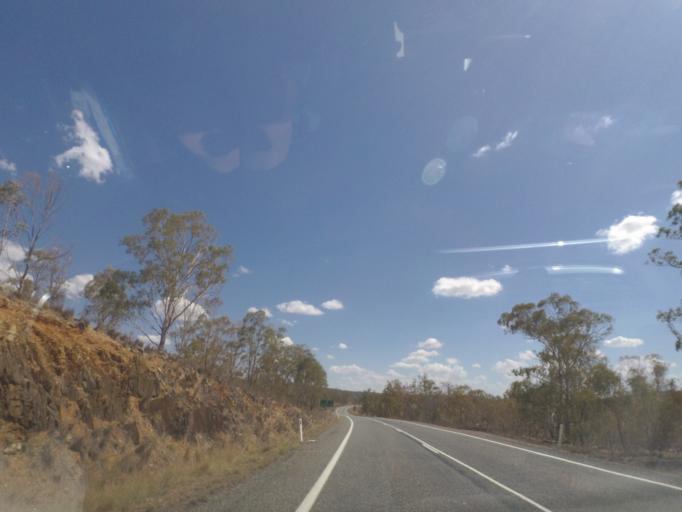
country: AU
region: Queensland
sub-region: Southern Downs
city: Warwick
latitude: -28.2105
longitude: 151.5648
